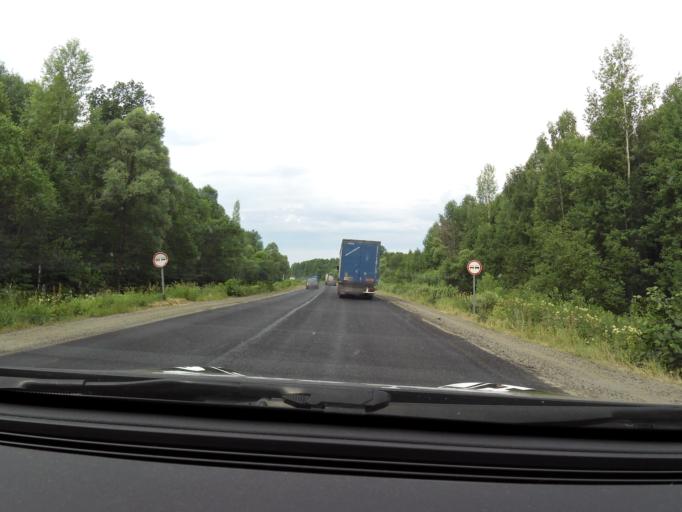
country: RU
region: Chelyabinsk
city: Asha
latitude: 54.8757
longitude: 57.1977
